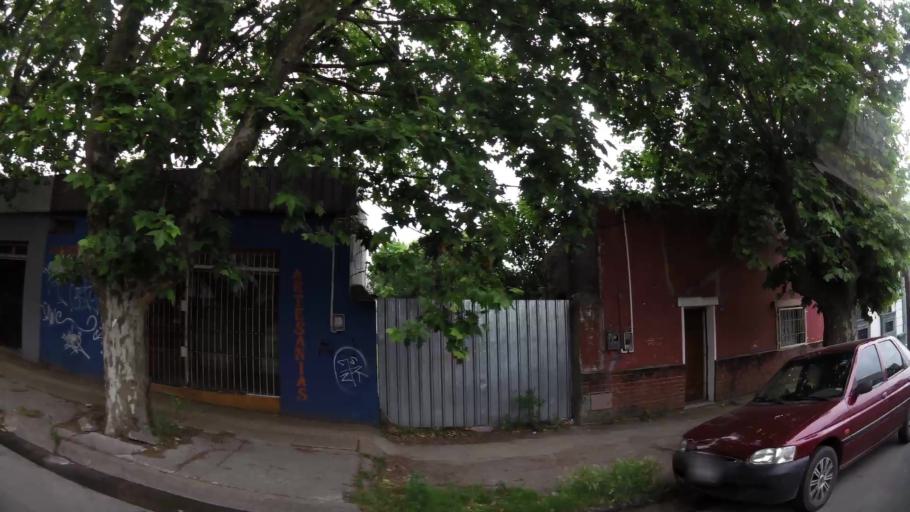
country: UY
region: Canelones
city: Las Piedras
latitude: -34.7248
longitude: -56.2139
